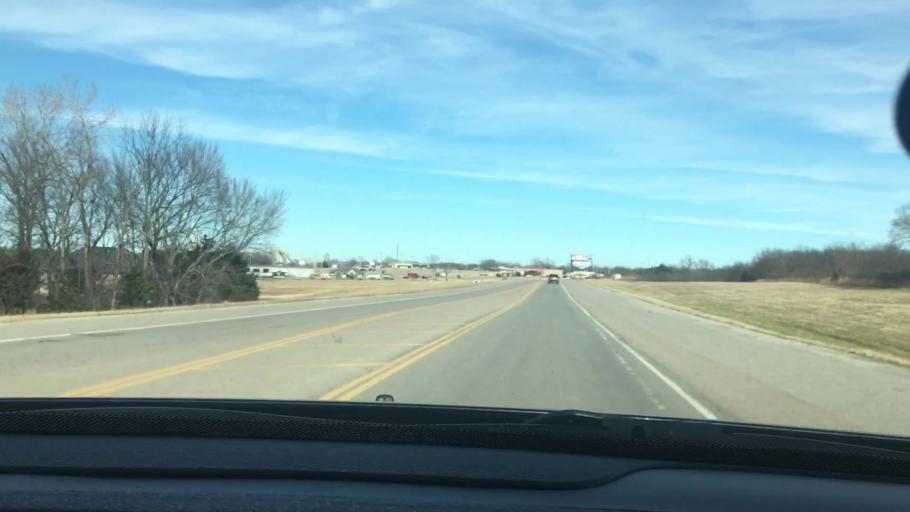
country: US
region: Oklahoma
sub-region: Pontotoc County
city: Ada
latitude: 34.7455
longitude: -96.7049
